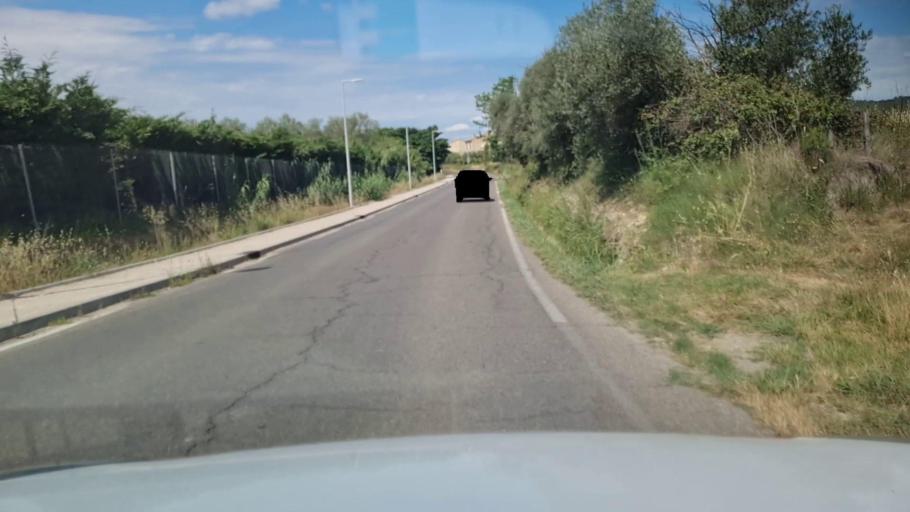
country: FR
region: Languedoc-Roussillon
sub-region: Departement du Gard
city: Clarensac
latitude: 43.8281
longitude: 4.2298
